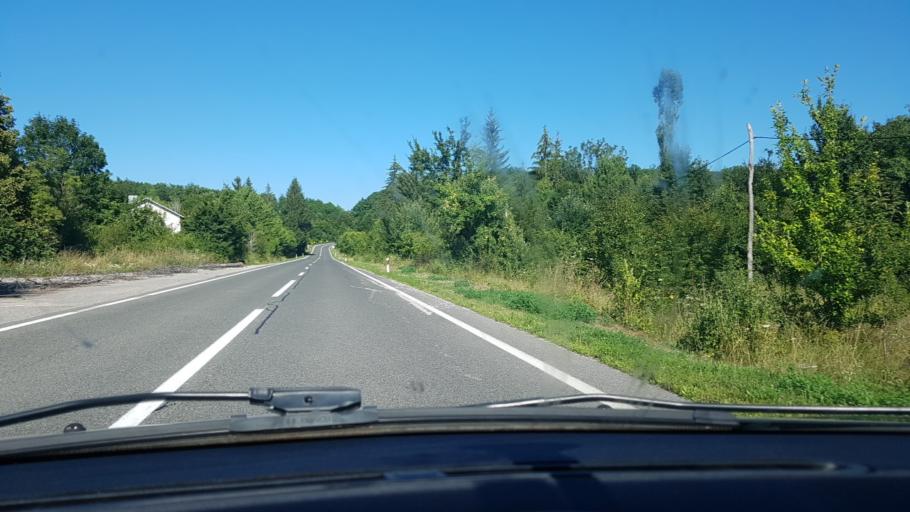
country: HR
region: Zadarska
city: Starigrad
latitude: 44.4285
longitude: 15.5435
